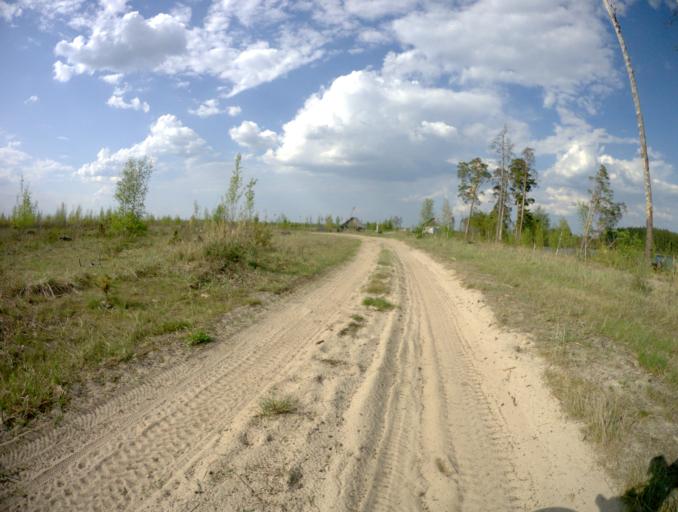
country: RU
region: Ivanovo
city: Talitsy
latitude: 56.4170
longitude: 42.2768
